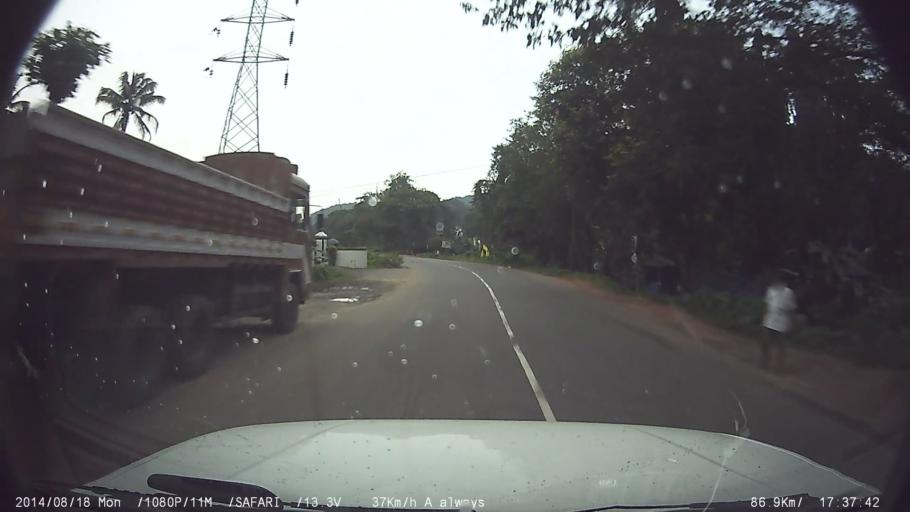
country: IN
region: Kerala
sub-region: Ernakulam
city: Muvattupuzha
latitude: 9.9110
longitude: 76.5836
